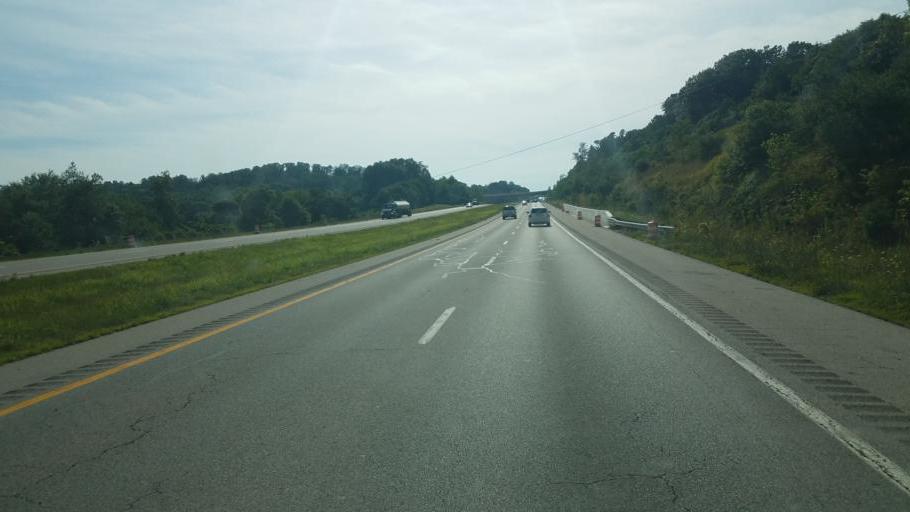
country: US
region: Ohio
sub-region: Fairfield County
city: Lancaster
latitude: 39.6677
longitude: -82.5896
